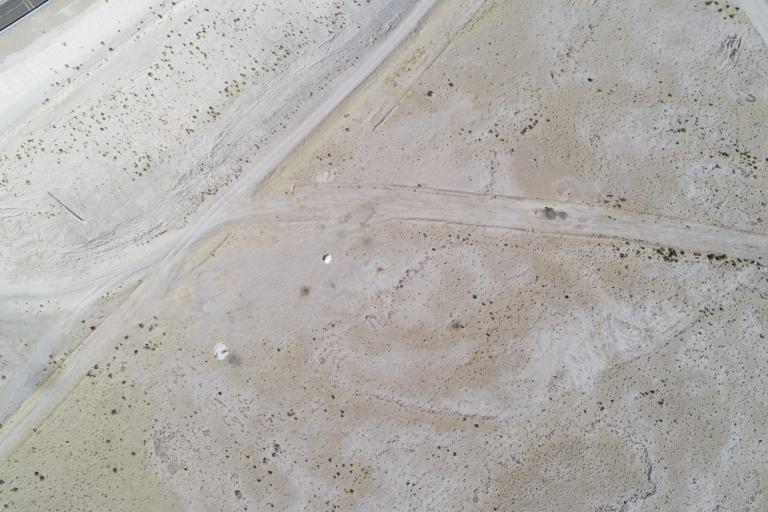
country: BO
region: Potosi
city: Colchani
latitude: -20.3536
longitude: -66.9039
